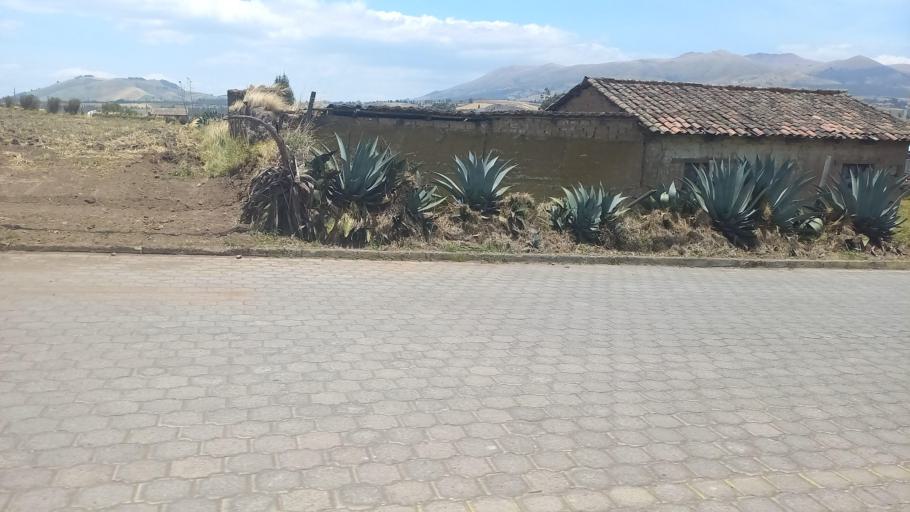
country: EC
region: Pichincha
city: Cayambe
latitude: 0.1433
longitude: -78.0700
